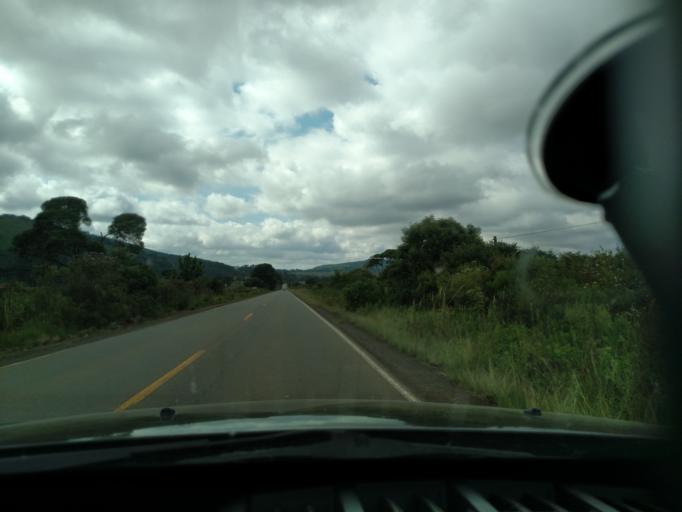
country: BR
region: Santa Catarina
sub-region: Lages
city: Lages
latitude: -27.8531
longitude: -50.2206
